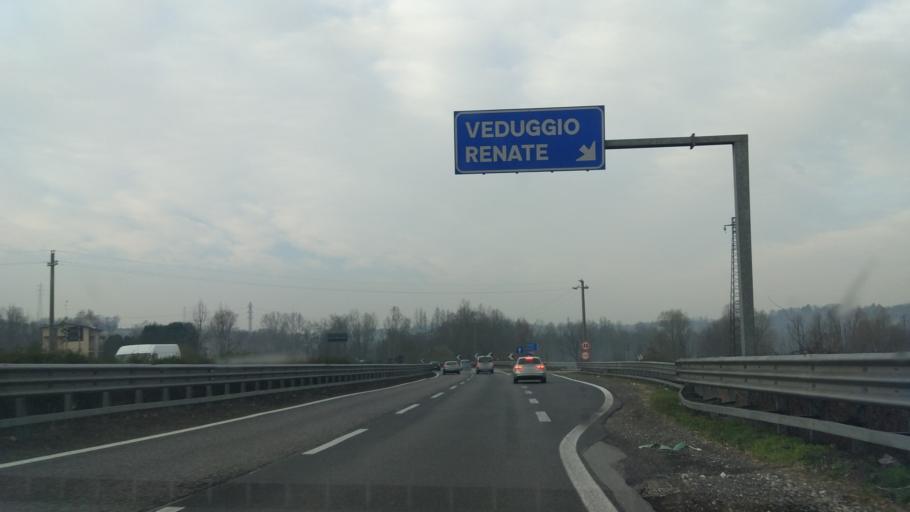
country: IT
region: Lombardy
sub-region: Provincia di Monza e Brianza
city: Capriano
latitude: 45.7381
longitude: 9.2512
